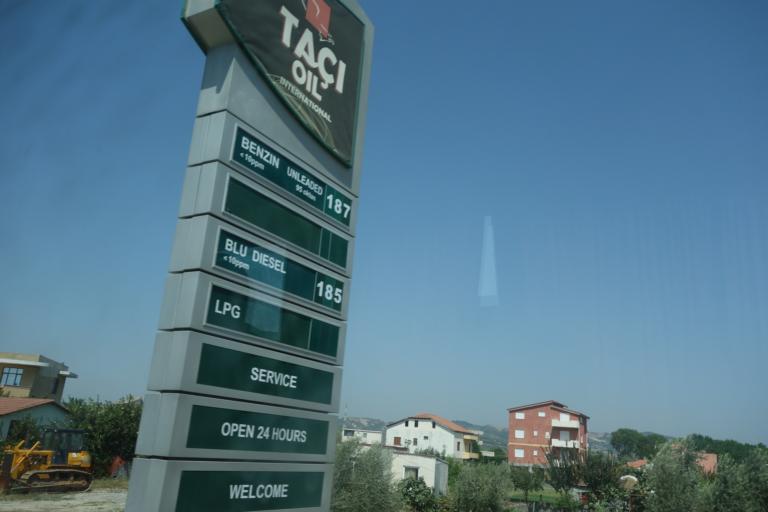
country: AL
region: Tirane
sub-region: Rrethi i Tiranes
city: Shengjergj
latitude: 41.2003
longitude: 19.5370
